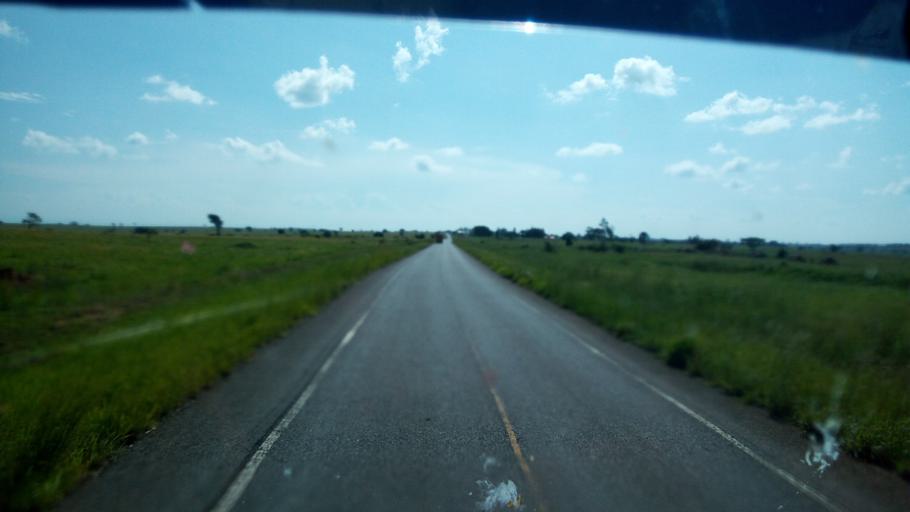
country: UG
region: Northern Region
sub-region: Nwoya District
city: Nwoya
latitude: 2.5639
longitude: 31.6506
